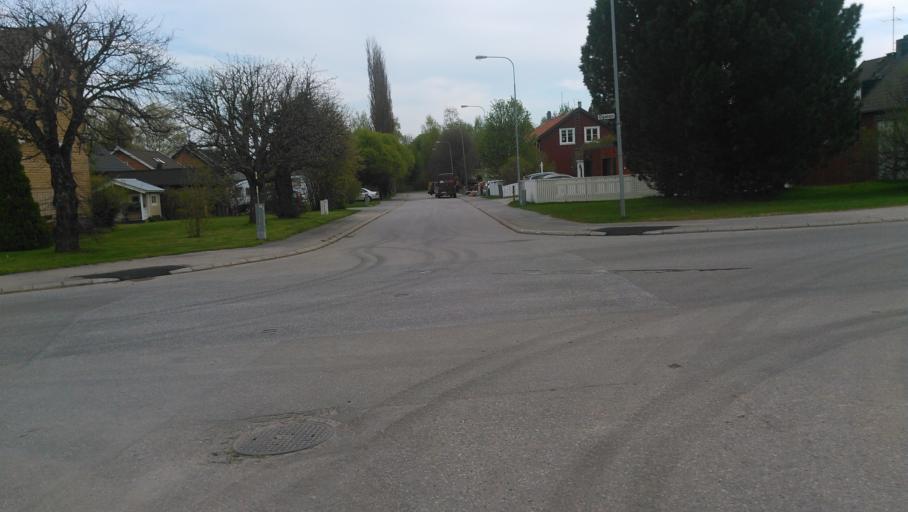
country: SE
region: Vaesterbotten
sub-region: Umea Kommun
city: Umea
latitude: 63.8108
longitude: 20.2698
